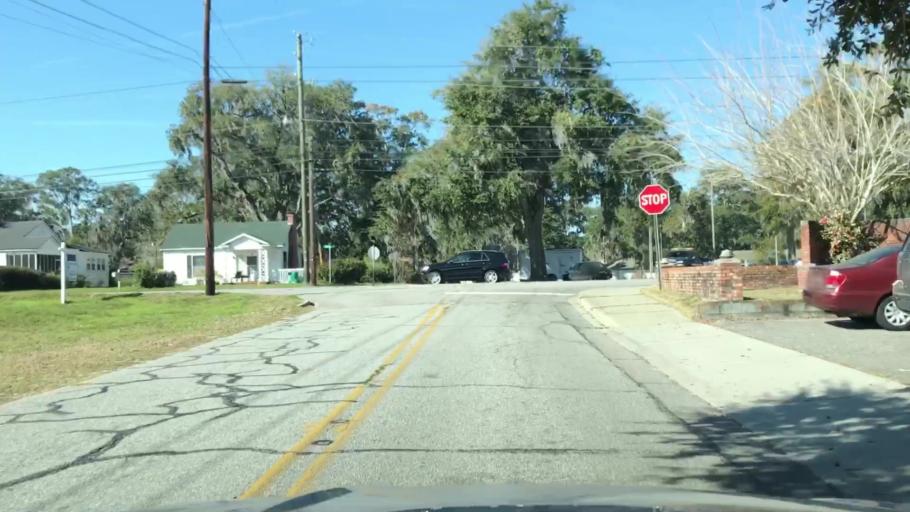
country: US
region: South Carolina
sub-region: Beaufort County
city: Beaufort
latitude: 32.4356
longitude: -80.6857
